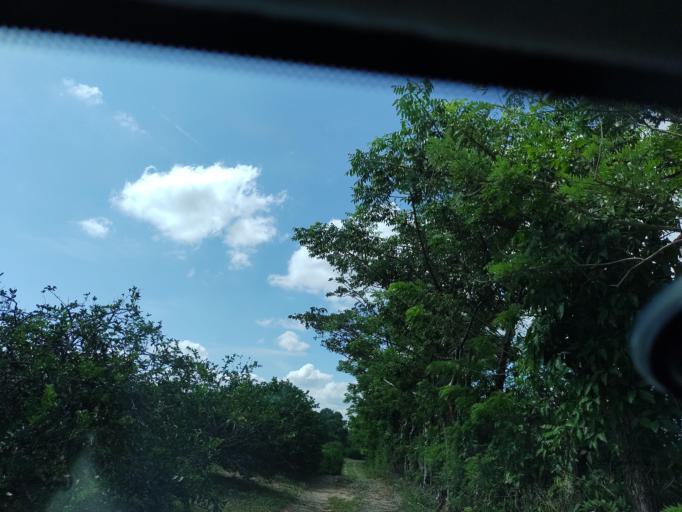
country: MX
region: Veracruz
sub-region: Martinez de la Torre
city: El Progreso
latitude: 20.1144
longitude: -97.0045
